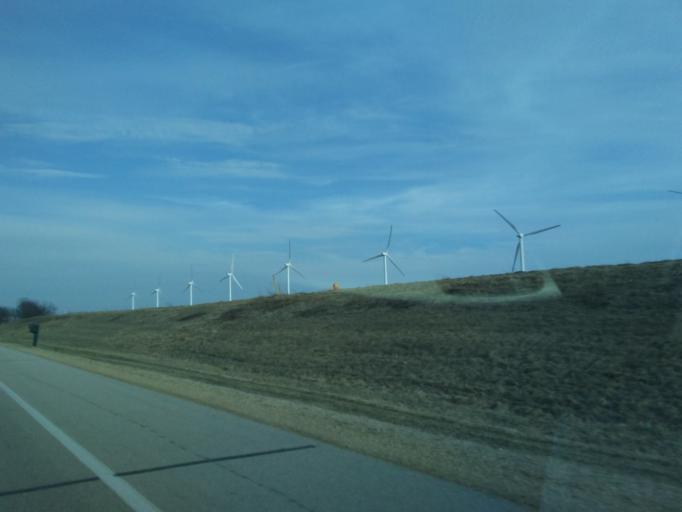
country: US
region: Wisconsin
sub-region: Grant County
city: Muscoda
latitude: 42.9666
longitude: -90.3847
